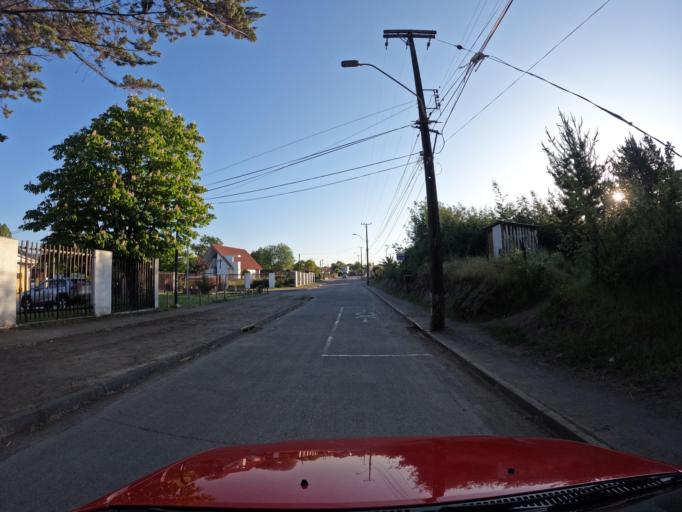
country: CL
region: Biobio
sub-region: Provincia de Concepcion
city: Lota
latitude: -37.1680
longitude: -72.9467
